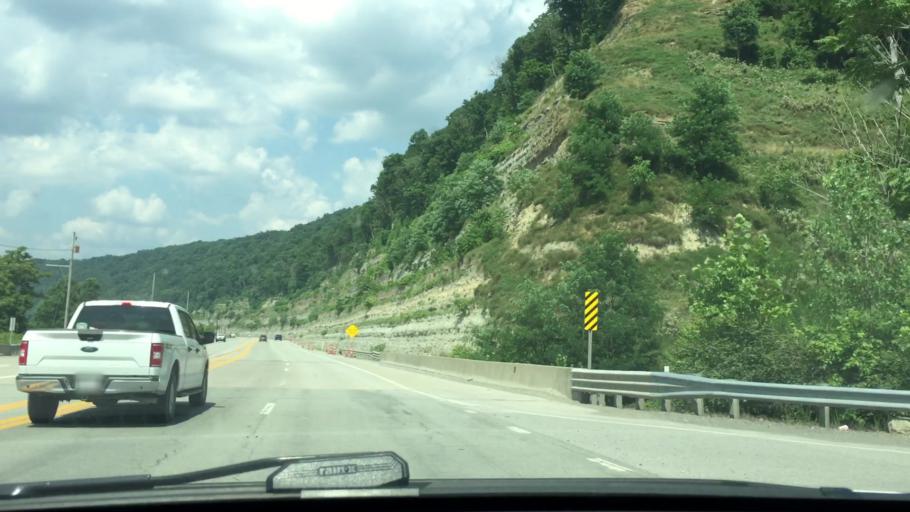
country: US
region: Ohio
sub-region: Belmont County
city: Powhatan Point
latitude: 39.8593
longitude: -80.7932
